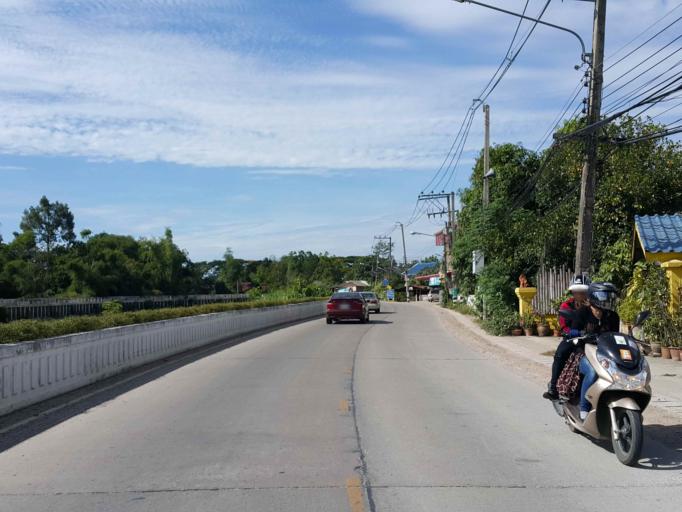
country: TH
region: Chiang Mai
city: Chiang Mai
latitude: 18.7508
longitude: 98.9876
